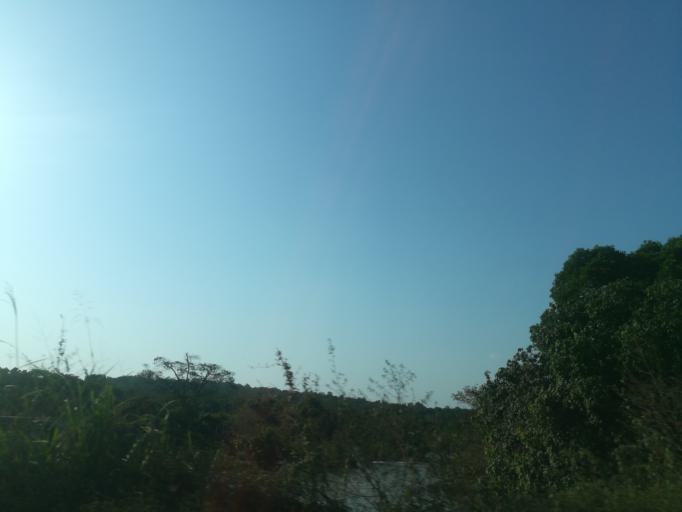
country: NG
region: Ogun
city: Abeokuta
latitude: 7.2178
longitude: 3.2963
